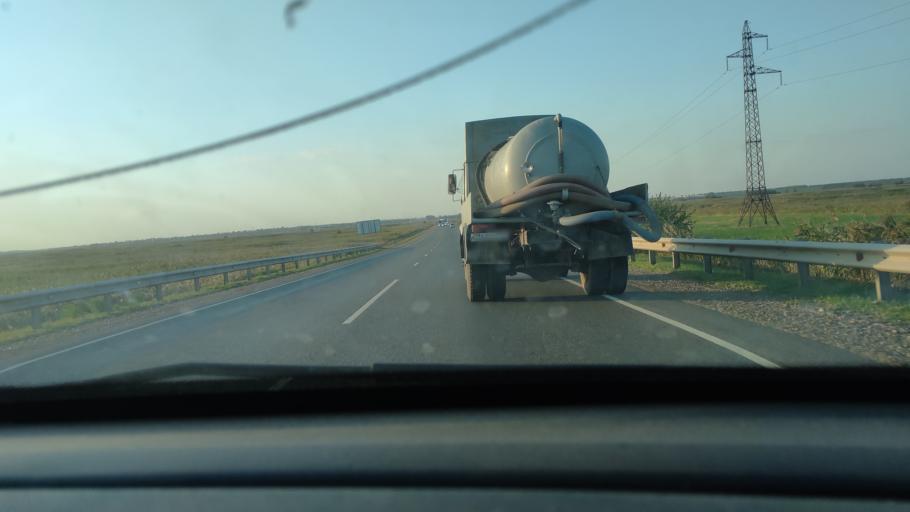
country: RU
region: Krasnodarskiy
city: Kanevskaya
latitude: 46.0806
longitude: 39.0124
